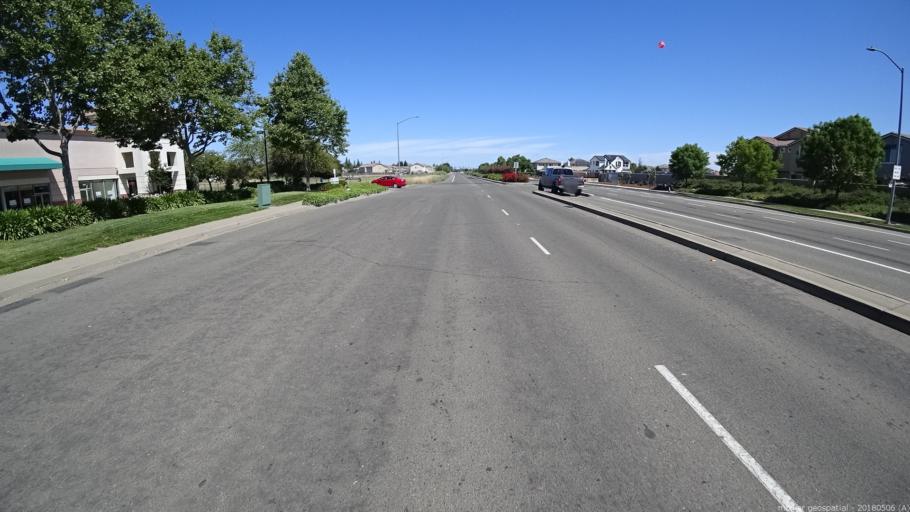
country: US
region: California
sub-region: Sacramento County
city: Laguna
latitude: 38.4394
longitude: -121.4179
